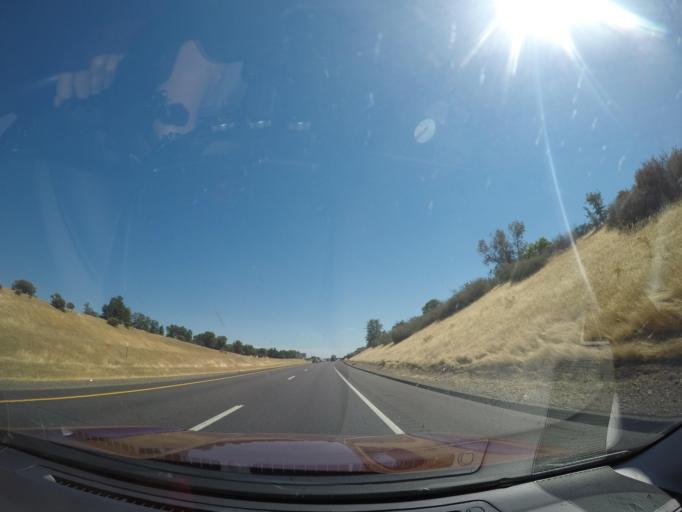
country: US
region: California
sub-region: Shasta County
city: Redding
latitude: 40.6032
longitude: -122.3609
